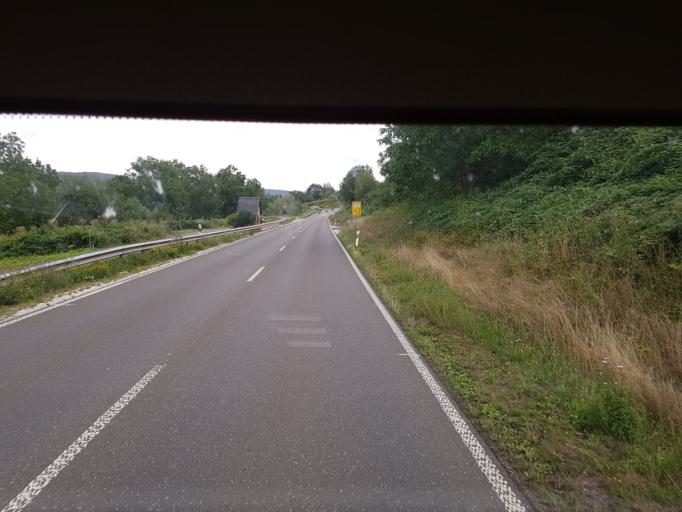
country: DE
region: Rheinland-Pfalz
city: Zeltingen-Rachtig
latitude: 49.9464
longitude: 7.0270
